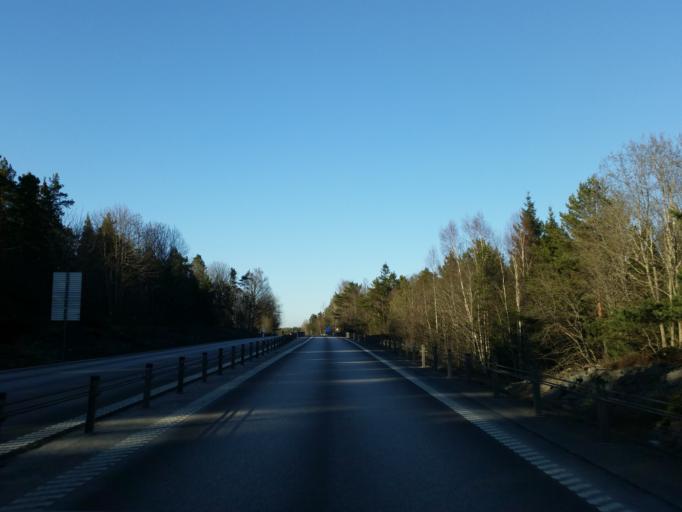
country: SE
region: Kalmar
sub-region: Oskarshamns Kommun
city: Oskarshamn
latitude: 57.2917
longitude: 16.4580
